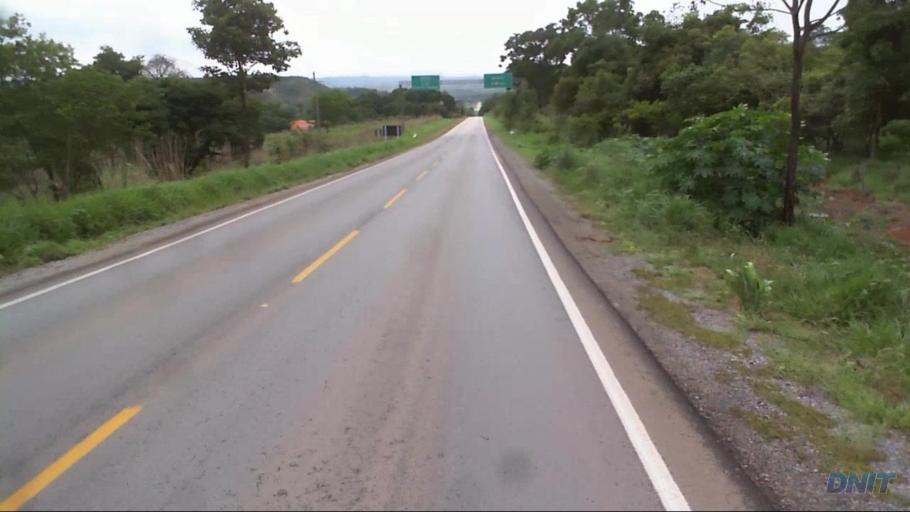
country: BR
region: Goias
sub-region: Padre Bernardo
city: Padre Bernardo
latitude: -15.5098
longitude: -48.1967
